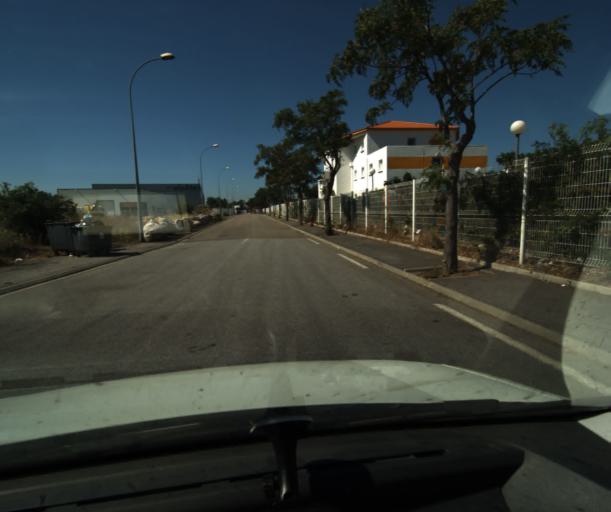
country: FR
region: Languedoc-Roussillon
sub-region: Departement des Pyrenees-Orientales
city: Rivesaltes
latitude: 42.7794
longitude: 2.8999
